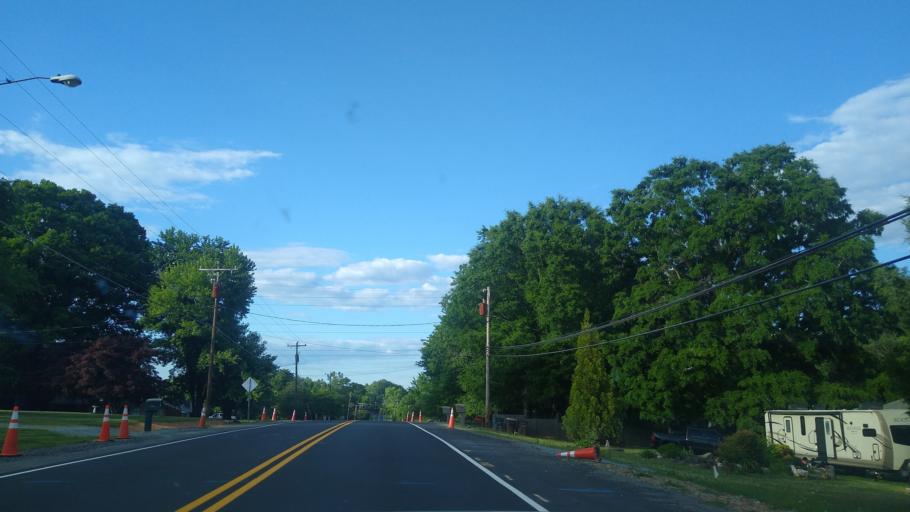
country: US
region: North Carolina
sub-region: Guilford County
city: McLeansville
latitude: 36.1626
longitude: -79.7320
